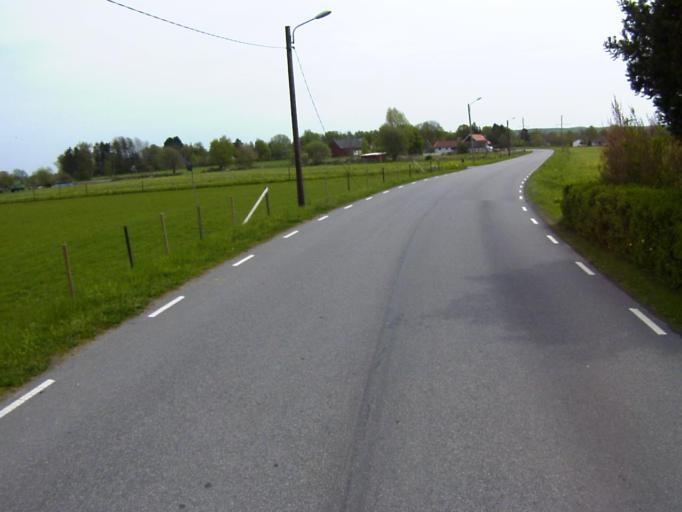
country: SE
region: Skane
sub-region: Kristianstads Kommun
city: Onnestad
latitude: 55.9413
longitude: 13.9522
